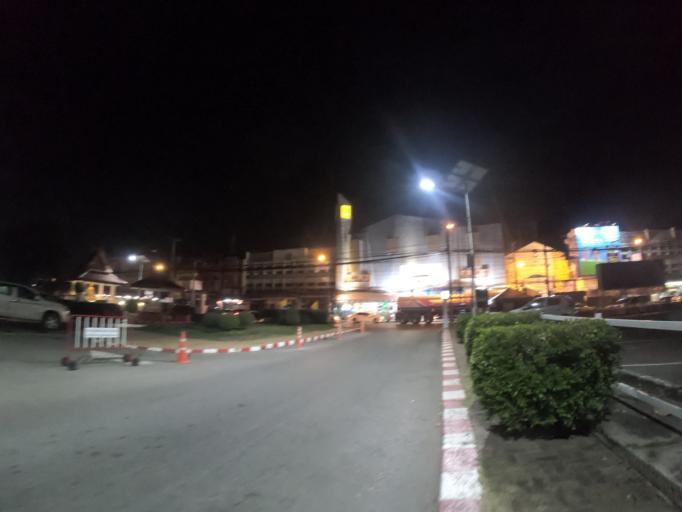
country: TH
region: Khon Kaen
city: Khon Kaen
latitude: 16.4288
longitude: 102.8356
